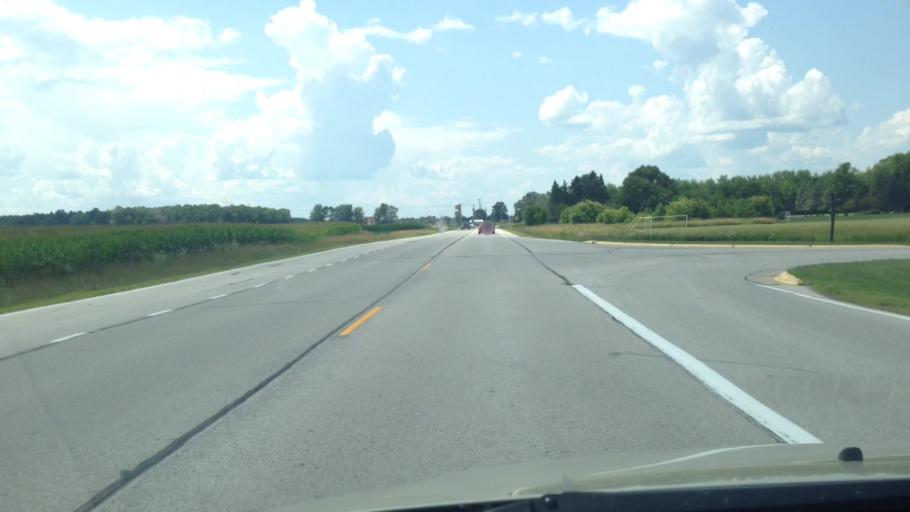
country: US
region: Wisconsin
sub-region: Brown County
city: Pulaski
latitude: 44.6566
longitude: -88.2382
